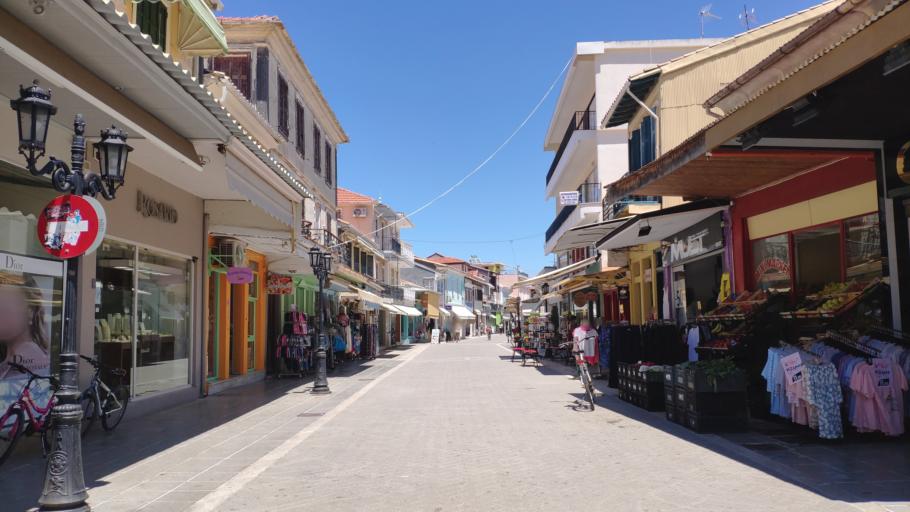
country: GR
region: Ionian Islands
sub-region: Lefkada
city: Lefkada
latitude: 38.8329
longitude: 20.7067
